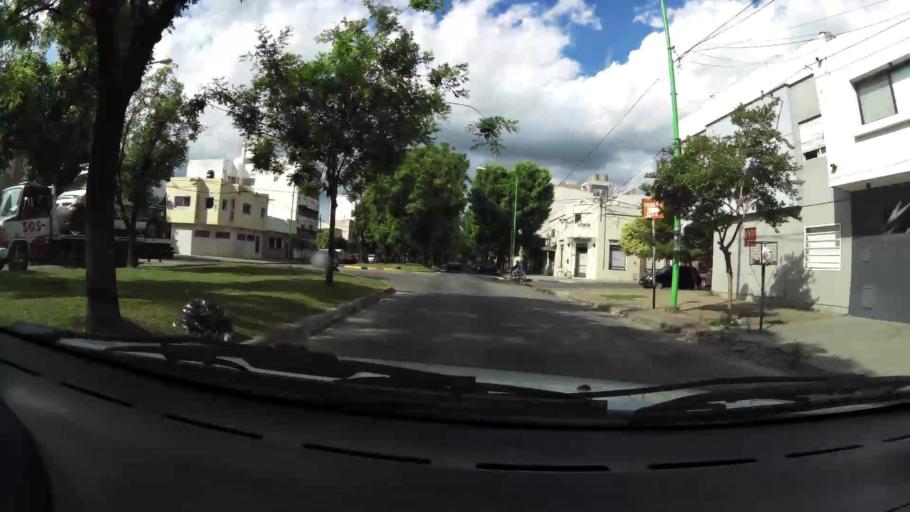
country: AR
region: Buenos Aires
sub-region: Partido de La Plata
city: La Plata
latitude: -34.9196
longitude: -57.9277
